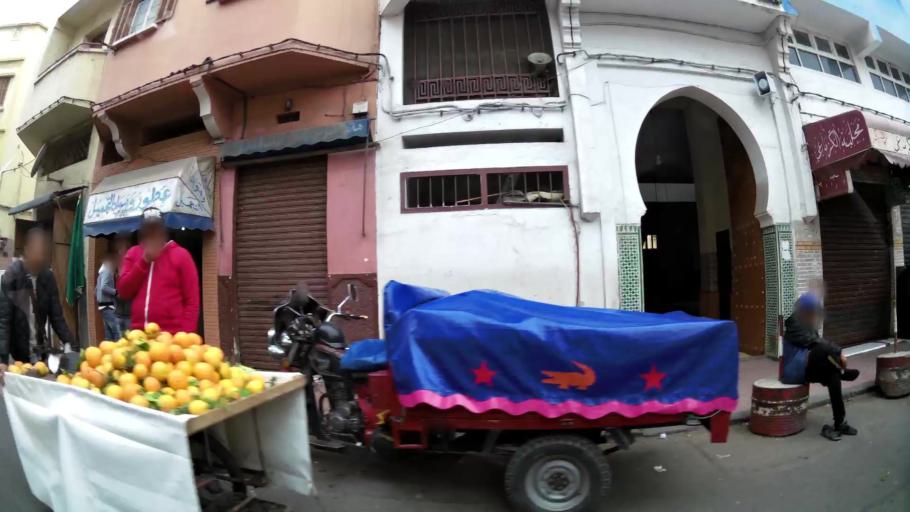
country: MA
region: Grand Casablanca
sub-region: Casablanca
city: Casablanca
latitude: 33.5675
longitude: -7.6083
